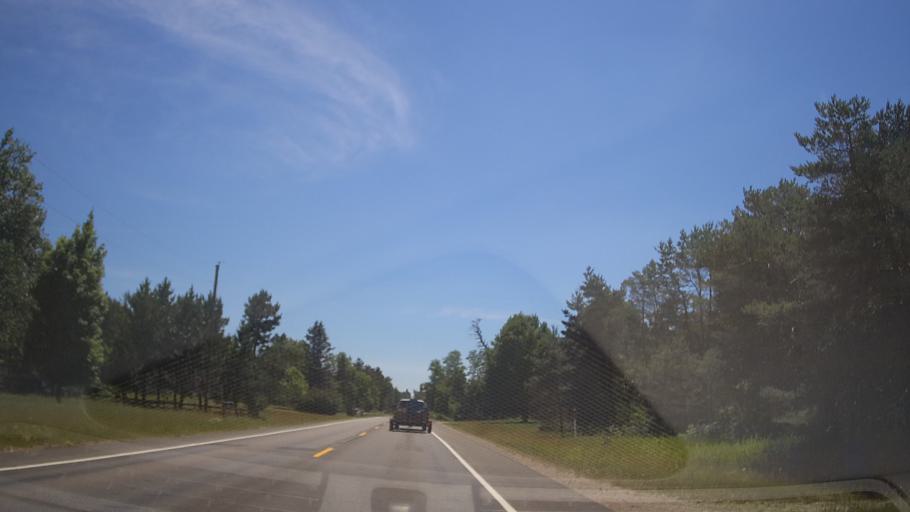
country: US
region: Michigan
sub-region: Grand Traverse County
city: Traverse City
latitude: 44.6411
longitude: -85.6964
